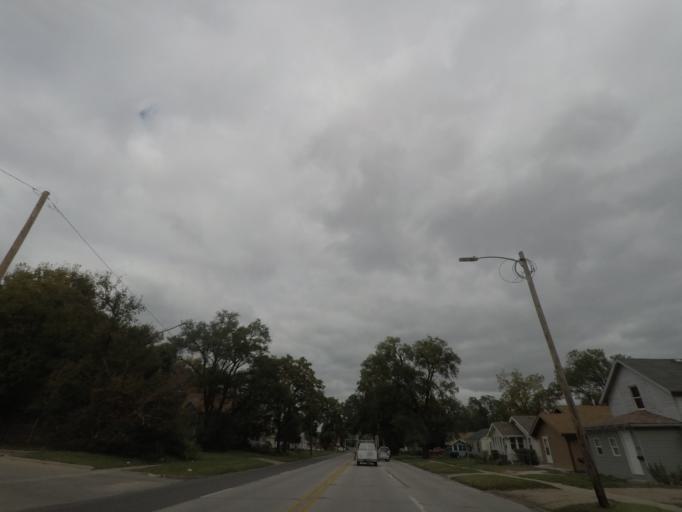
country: US
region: Iowa
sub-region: Polk County
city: Des Moines
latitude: 41.6030
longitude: -93.6005
